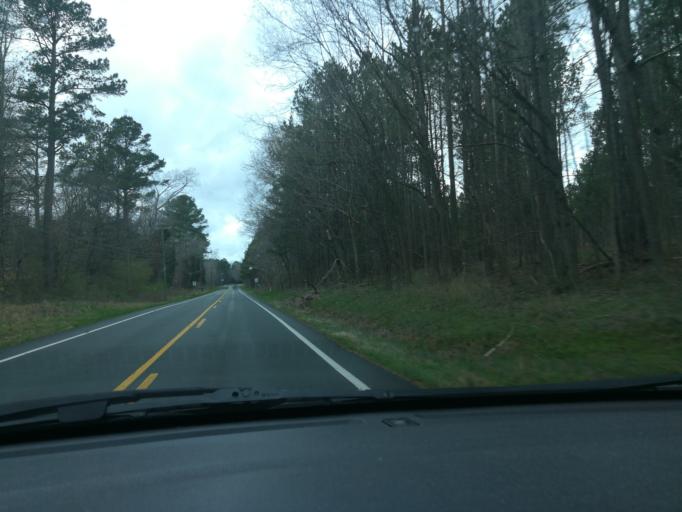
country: US
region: North Carolina
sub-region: Orange County
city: Hillsborough
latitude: 36.0345
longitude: -79.0493
